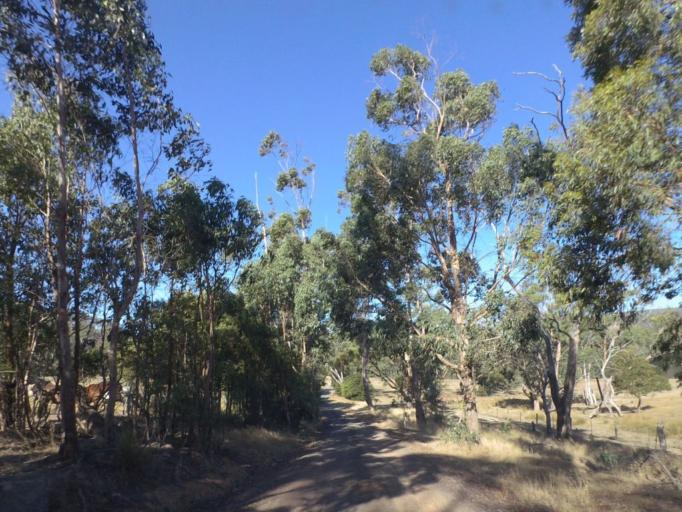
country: AU
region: Victoria
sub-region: Murrindindi
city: Kinglake West
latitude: -37.4599
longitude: 145.3938
